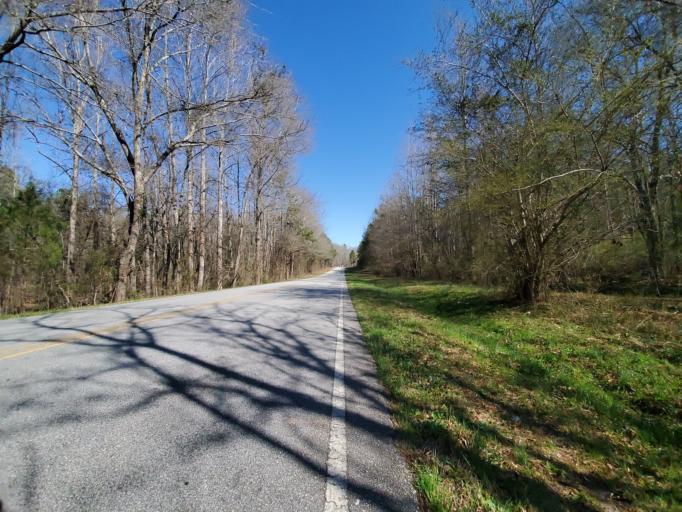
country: US
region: Georgia
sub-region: Oconee County
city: Bogart
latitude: 34.0005
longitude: -83.4955
